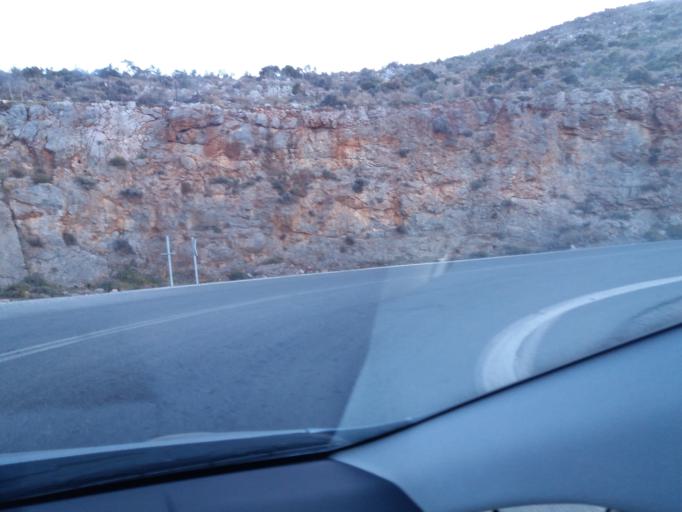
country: GR
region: Crete
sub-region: Nomos Irakleiou
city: Mokhos
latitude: 35.2749
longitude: 25.4293
